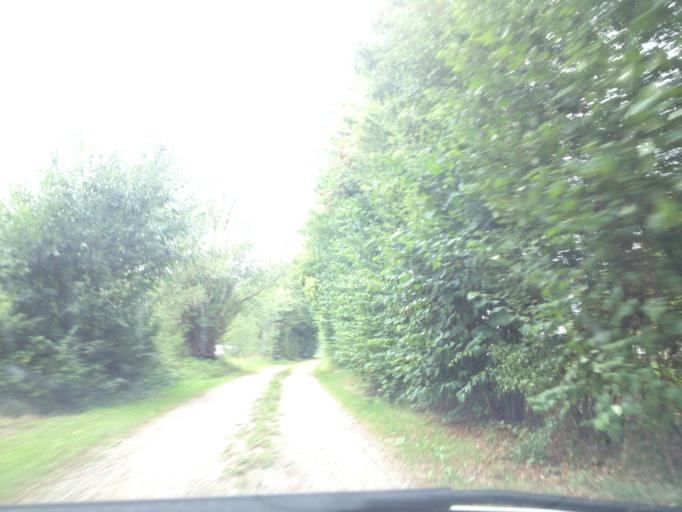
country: DK
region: South Denmark
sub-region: Haderslev Kommune
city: Starup
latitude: 55.2980
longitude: 9.5605
